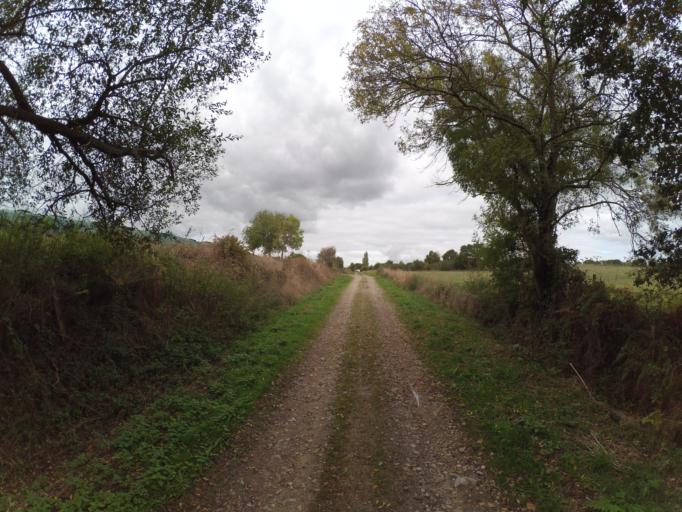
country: FR
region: Pays de la Loire
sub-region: Departement de la Loire-Atlantique
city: Remouille
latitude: 47.0527
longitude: -1.3567
